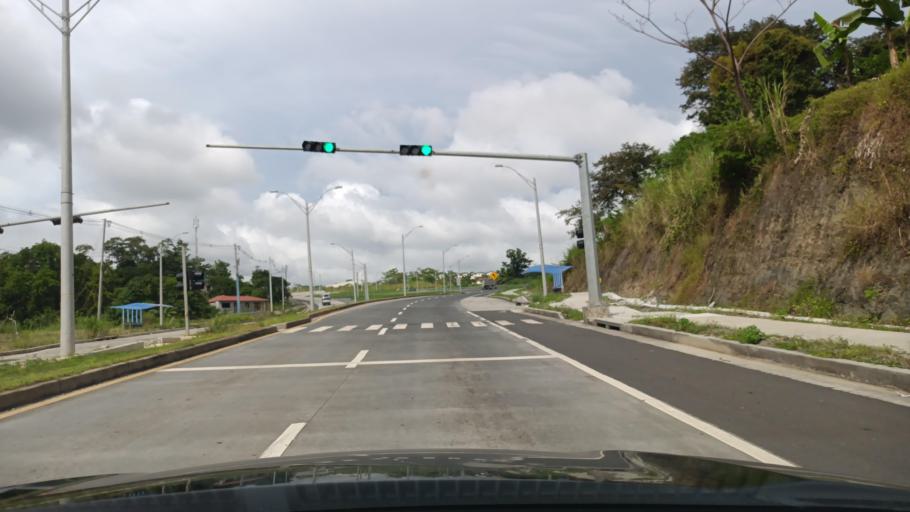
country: PA
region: Panama
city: Las Cumbres
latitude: 9.1001
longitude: -79.5154
